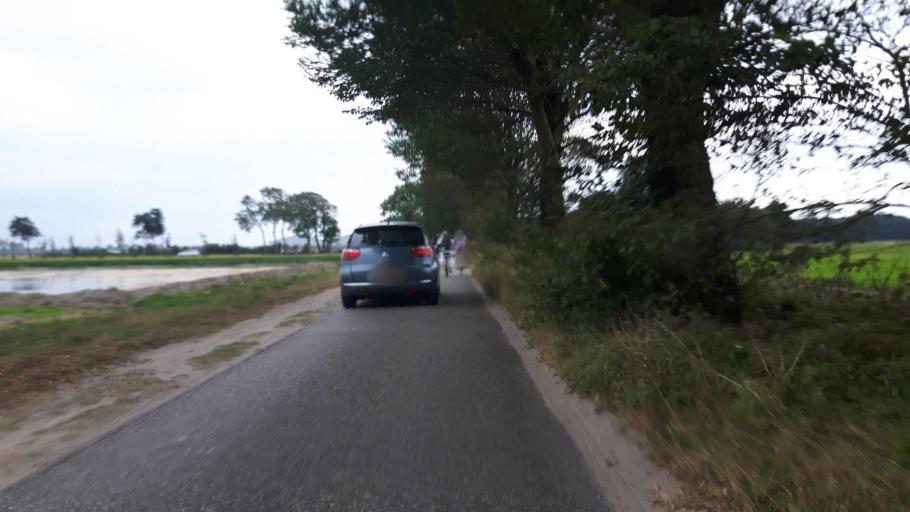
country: NL
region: South Holland
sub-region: Gemeente Hillegom
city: Hillegom
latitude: 52.3163
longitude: 4.5639
